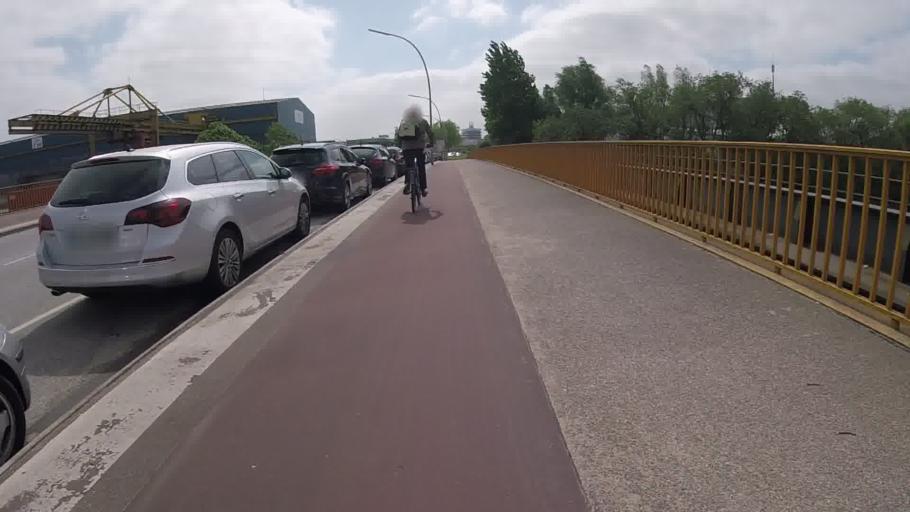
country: DE
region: Hamburg
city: Rothenburgsort
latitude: 53.5283
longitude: 10.0775
